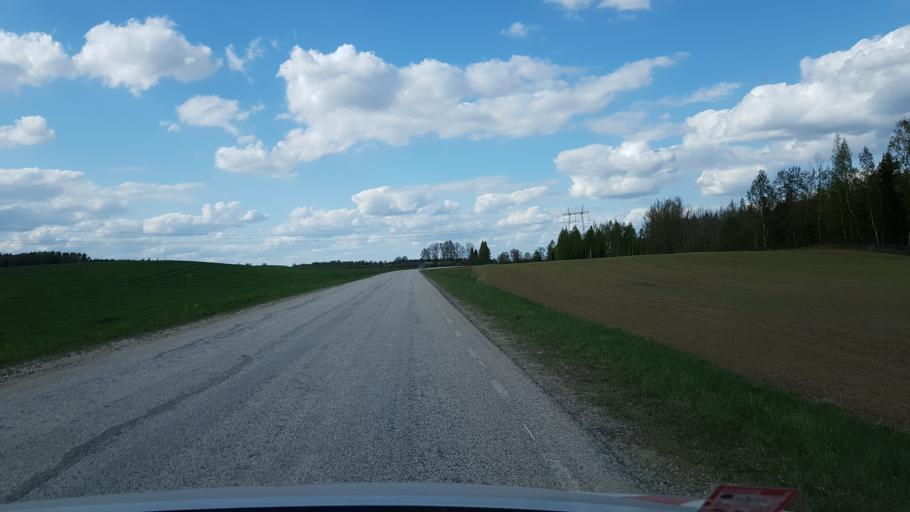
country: EE
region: Tartu
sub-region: UElenurme vald
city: Ulenurme
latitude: 58.2719
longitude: 26.9081
